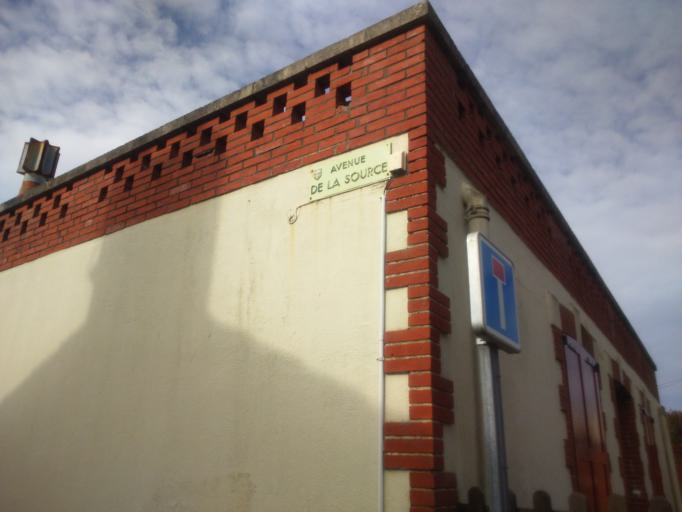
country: FR
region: Pays de la Loire
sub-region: Departement de la Loire-Atlantique
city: La Bernerie-en-Retz
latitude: 47.0836
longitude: -2.0410
